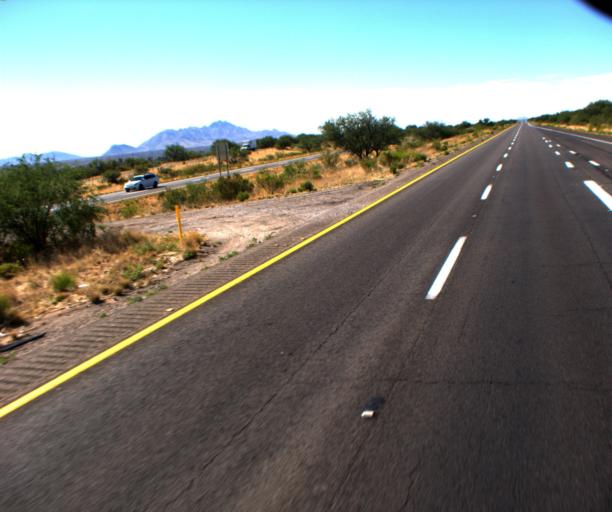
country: US
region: Arizona
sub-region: Santa Cruz County
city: Tubac
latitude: 31.6481
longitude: -111.0589
